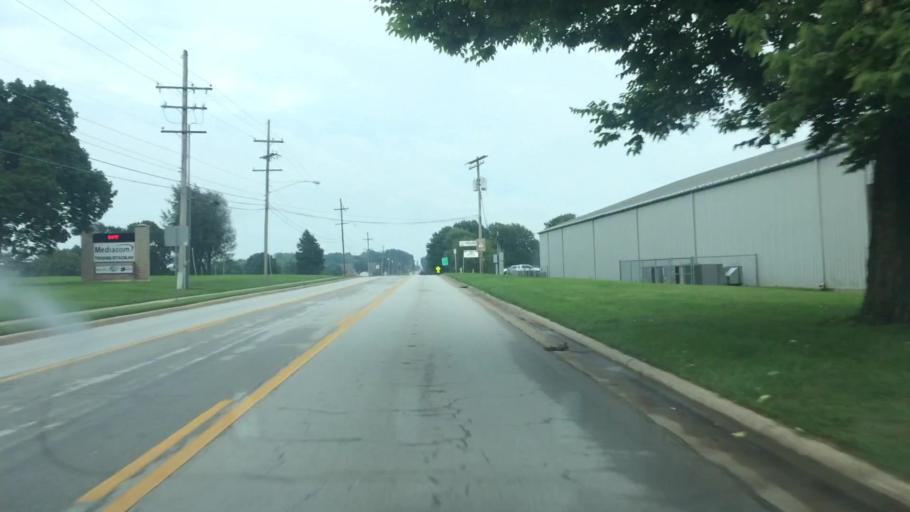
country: US
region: Missouri
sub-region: Greene County
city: Springfield
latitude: 37.2178
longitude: -93.2504
